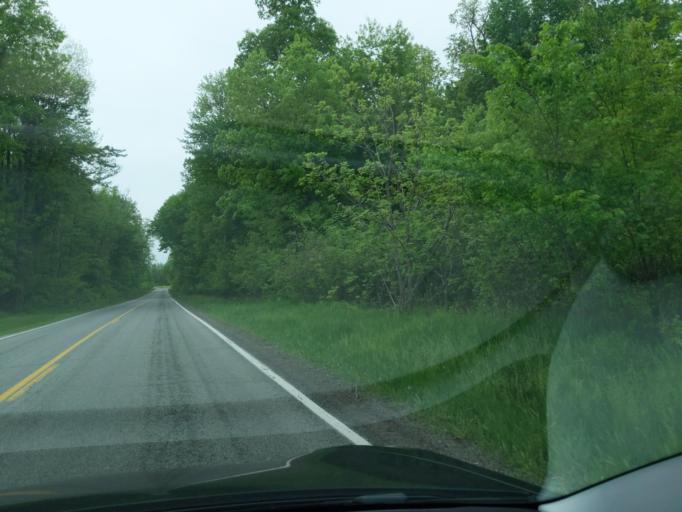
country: US
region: Michigan
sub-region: Ingham County
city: Leslie
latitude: 42.4463
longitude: -84.3504
